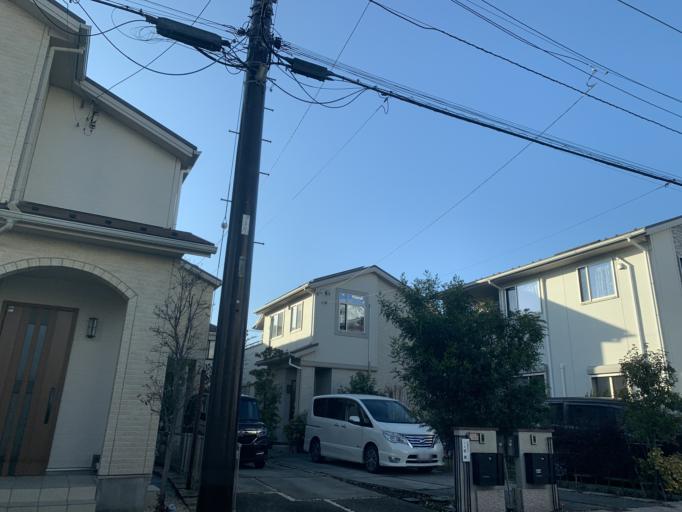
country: JP
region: Chiba
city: Nagareyama
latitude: 35.8994
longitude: 139.9321
